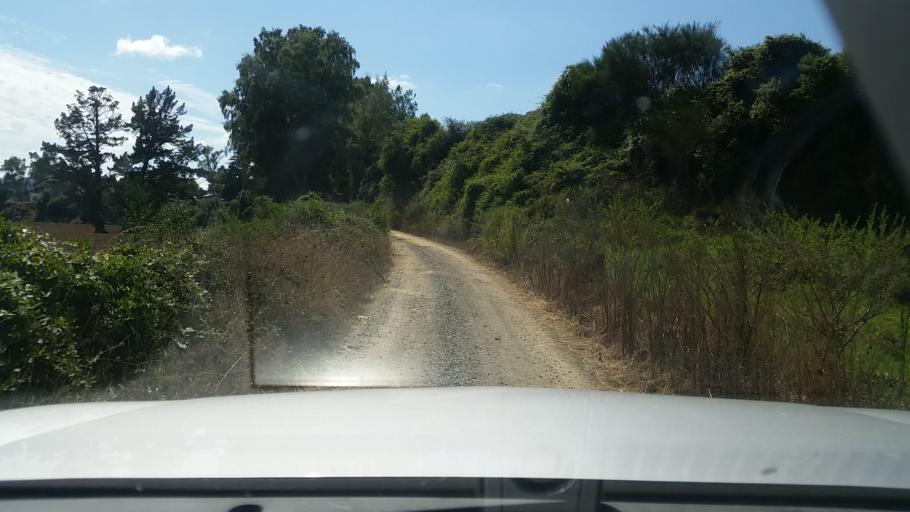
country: NZ
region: Nelson
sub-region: Nelson City
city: Nelson
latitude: -41.2500
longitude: 173.5842
